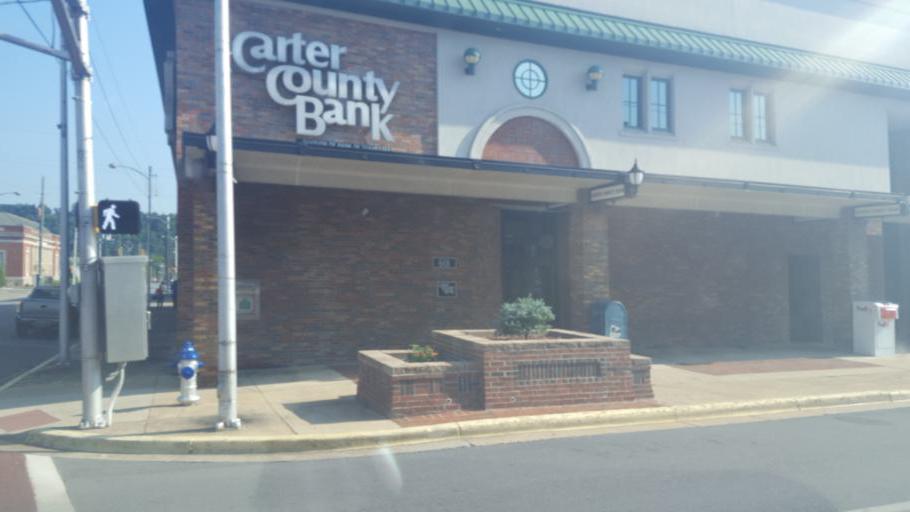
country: US
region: Tennessee
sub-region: Carter County
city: Elizabethton
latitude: 36.3480
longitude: -82.2145
